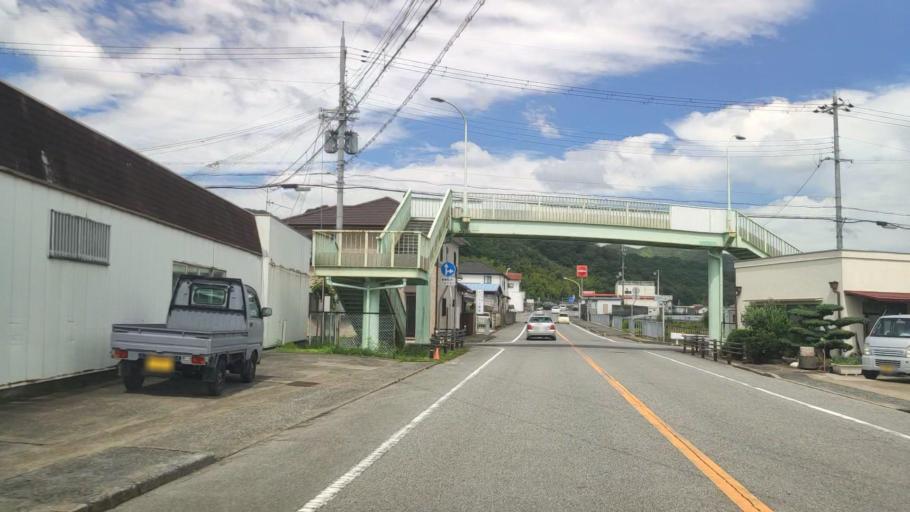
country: JP
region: Hyogo
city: Nishiwaki
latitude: 35.0150
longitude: 134.9590
